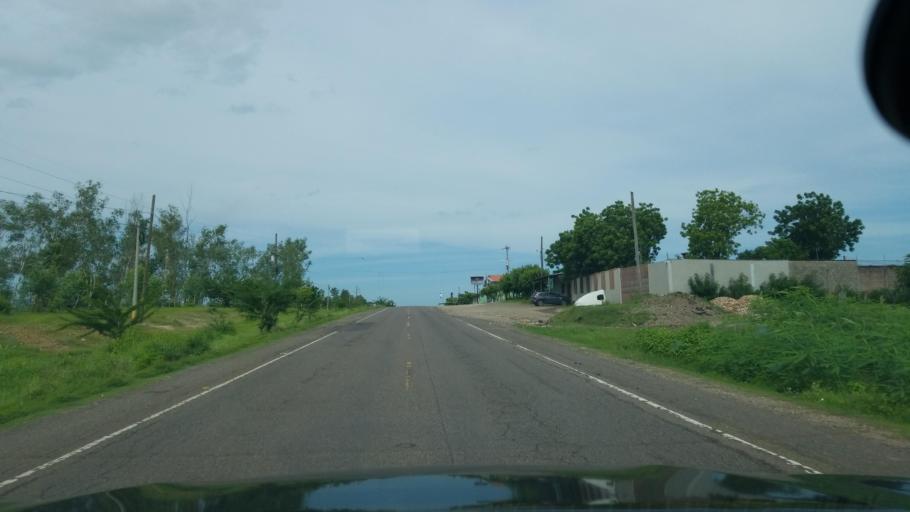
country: HN
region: Choluteca
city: Santa Ana de Yusguare
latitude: 13.3406
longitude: -87.1257
